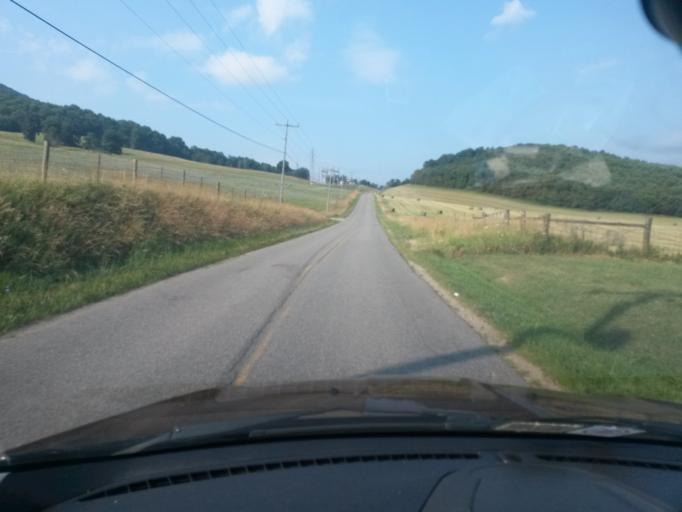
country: US
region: Virginia
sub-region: Giles County
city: Narrows
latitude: 37.3762
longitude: -80.7941
